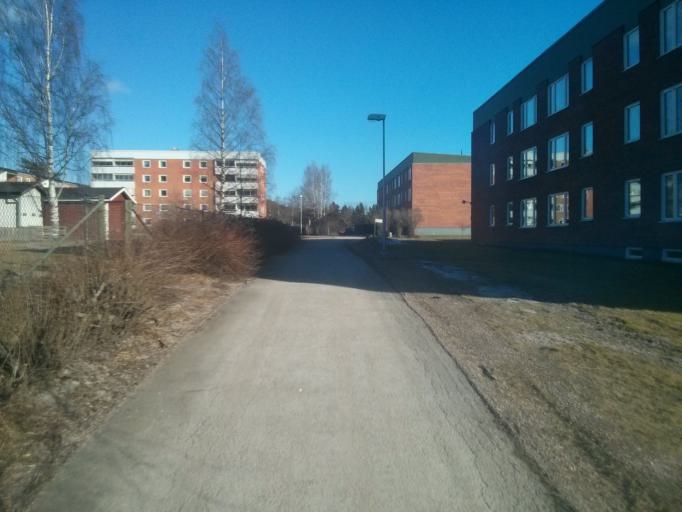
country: SE
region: Vaesternorrland
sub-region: Sundsvalls Kommun
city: Kvissleby
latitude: 62.2983
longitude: 17.3801
